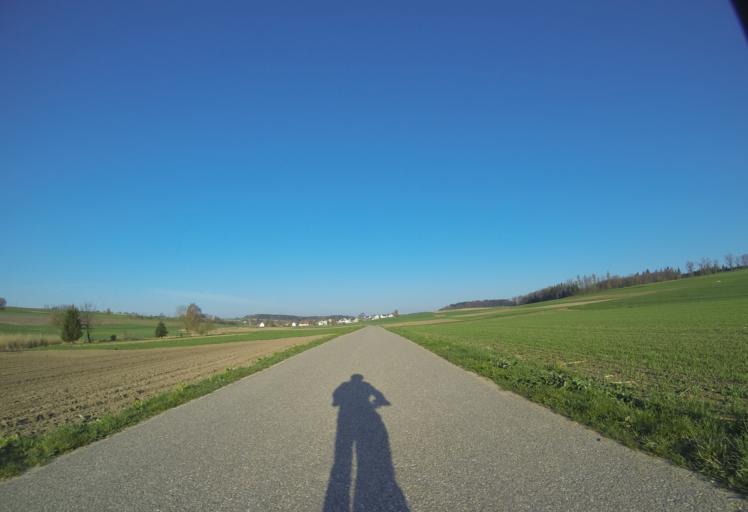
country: DE
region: Baden-Wuerttemberg
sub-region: Tuebingen Region
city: Erbach
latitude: 48.3305
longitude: 9.8682
